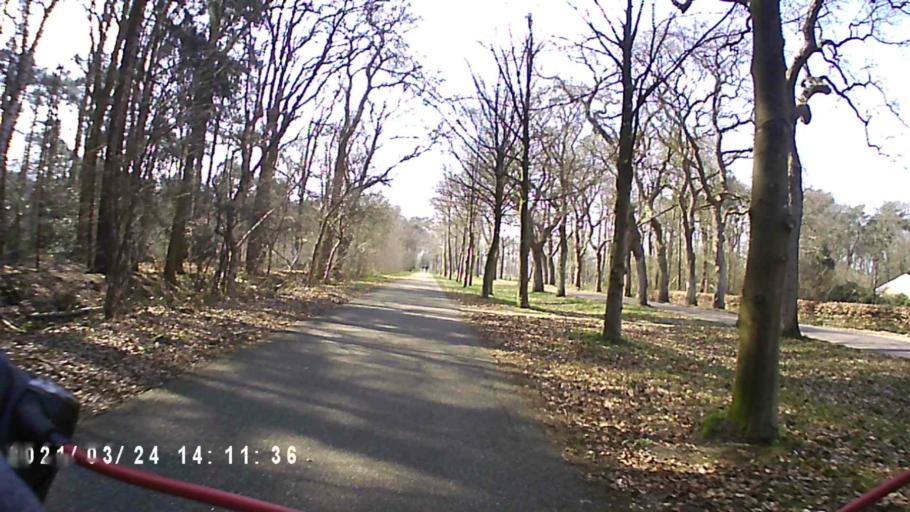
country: NL
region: Friesland
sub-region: Gemeente Smallingerland
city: Drachtstercompagnie
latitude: 53.0678
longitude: 6.2268
